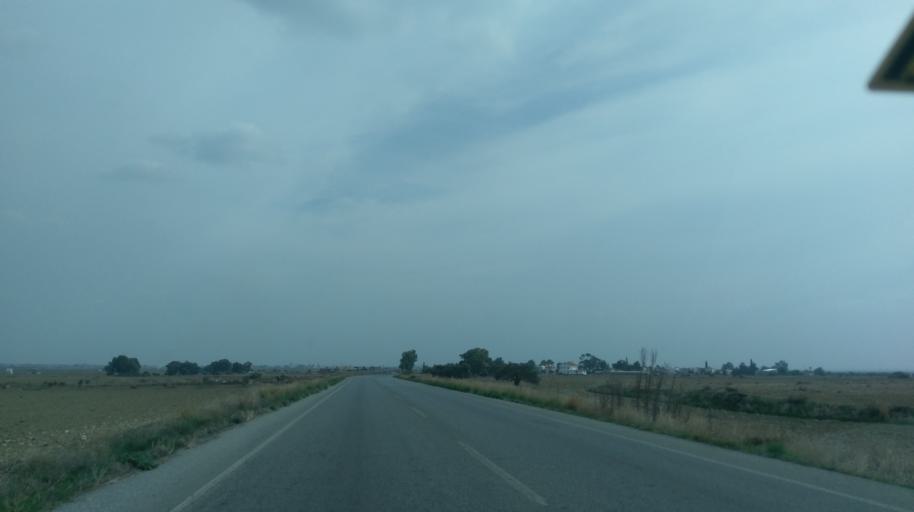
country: CY
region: Ammochostos
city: Lefkonoiko
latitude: 35.2582
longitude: 33.6768
